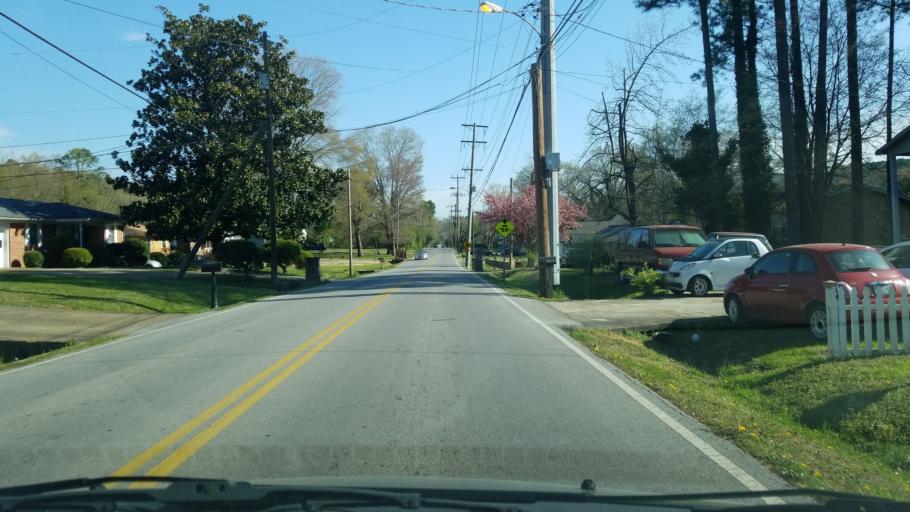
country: US
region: Tennessee
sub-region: Hamilton County
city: East Chattanooga
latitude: 35.0575
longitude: -85.2311
